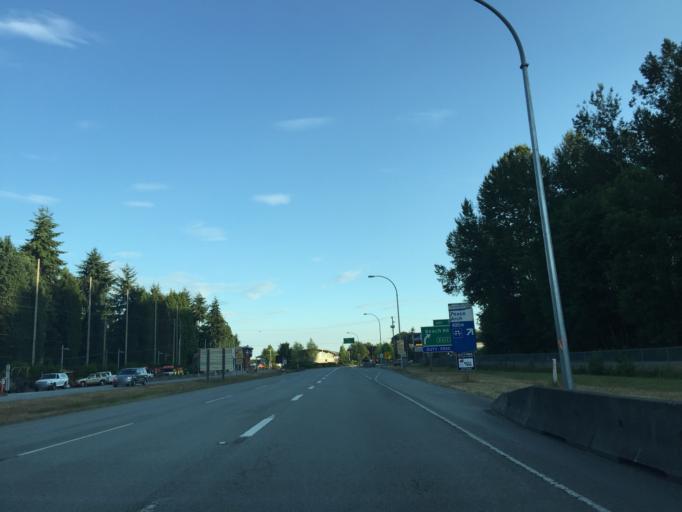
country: US
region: Washington
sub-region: Whatcom County
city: Blaine
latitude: 49.0088
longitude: -122.7577
